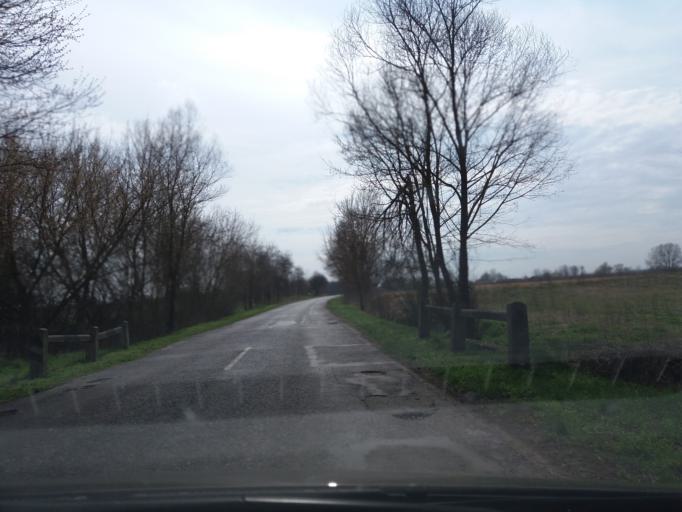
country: HU
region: Szabolcs-Szatmar-Bereg
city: Petnehaza
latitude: 48.0749
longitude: 22.0891
